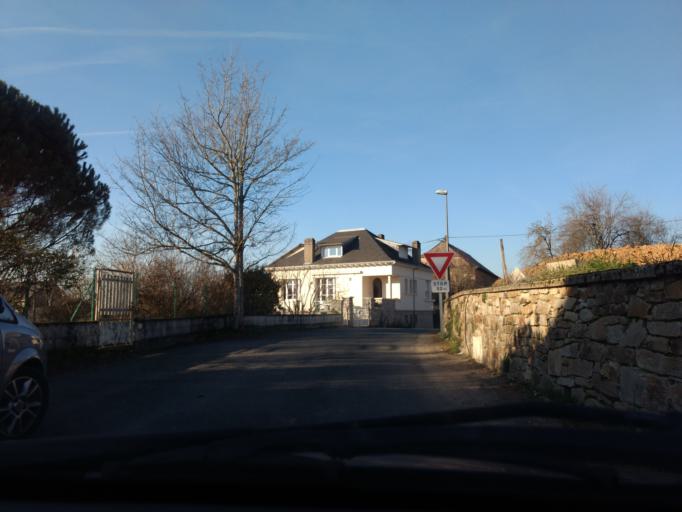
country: FR
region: Midi-Pyrenees
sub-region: Departement de l'Aveyron
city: Naucelle
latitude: 44.1973
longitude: 2.3389
